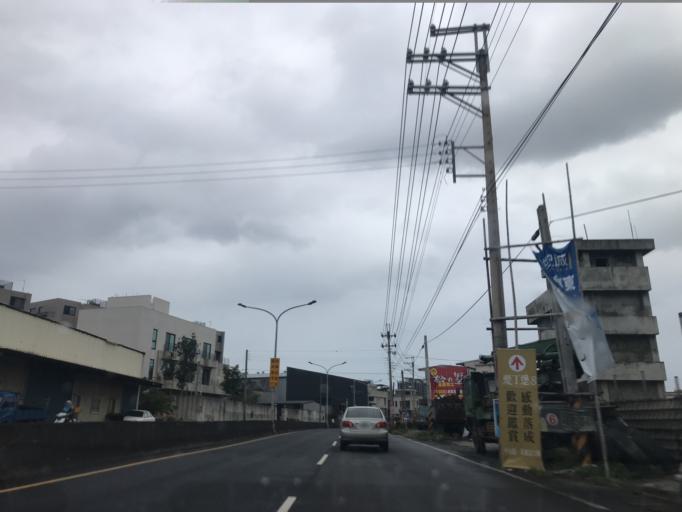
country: TW
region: Taiwan
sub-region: Hsinchu
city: Zhubei
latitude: 24.8312
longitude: 121.0337
